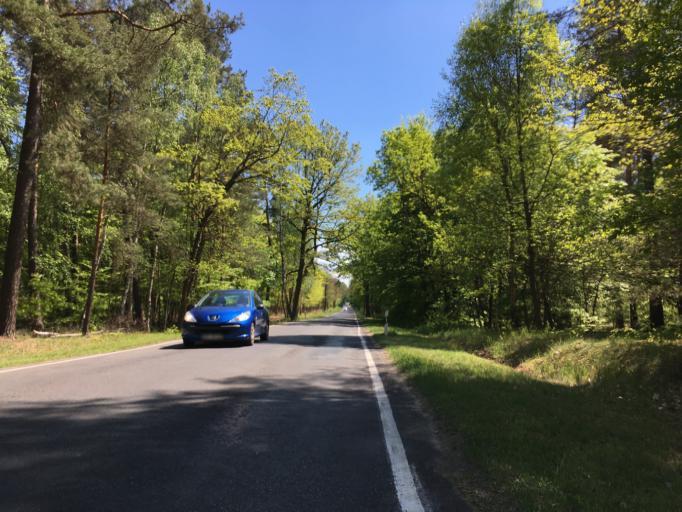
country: DE
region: Brandenburg
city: Bernau bei Berlin
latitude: 52.7121
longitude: 13.5799
